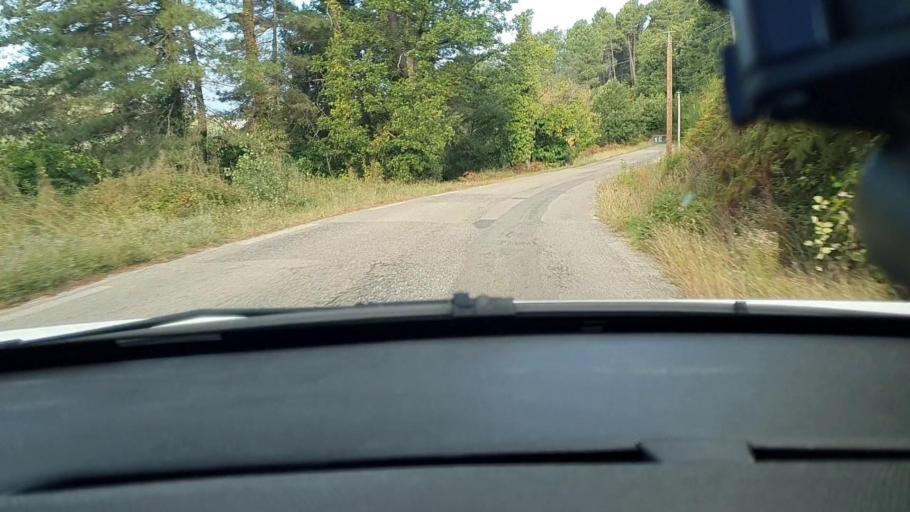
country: FR
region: Languedoc-Roussillon
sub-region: Departement du Gard
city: Besseges
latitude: 44.3253
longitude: 4.0162
